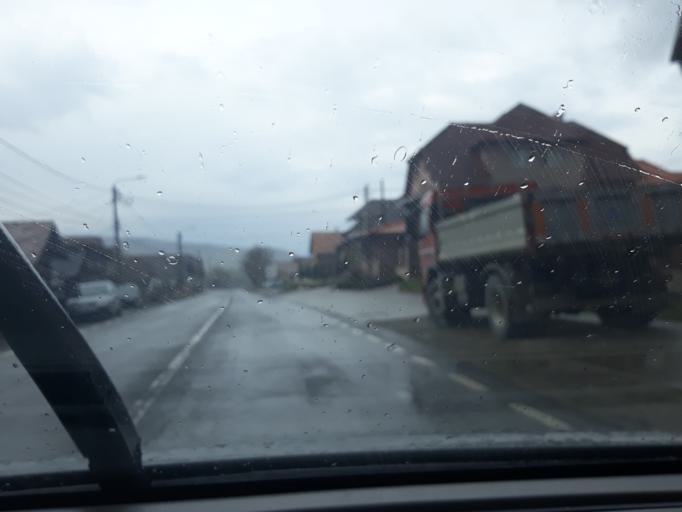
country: RO
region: Harghita
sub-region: Comuna Corund
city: Corund
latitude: 46.4777
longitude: 25.1754
